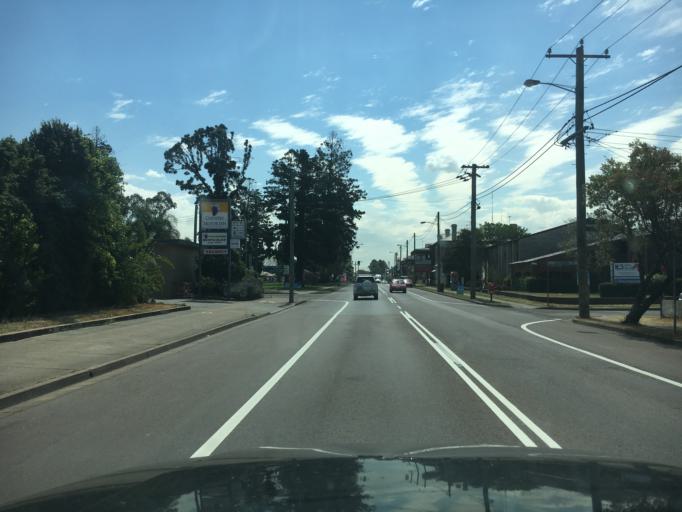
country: AU
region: New South Wales
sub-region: Singleton
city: Singleton
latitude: -32.5647
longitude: 151.1771
